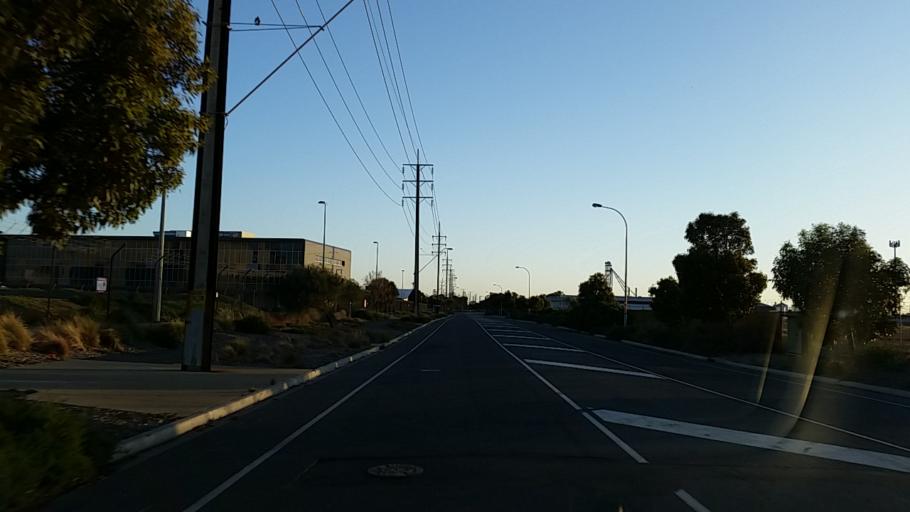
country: AU
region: South Australia
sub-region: Port Adelaide Enfield
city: Birkenhead
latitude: -34.7861
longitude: 138.5070
